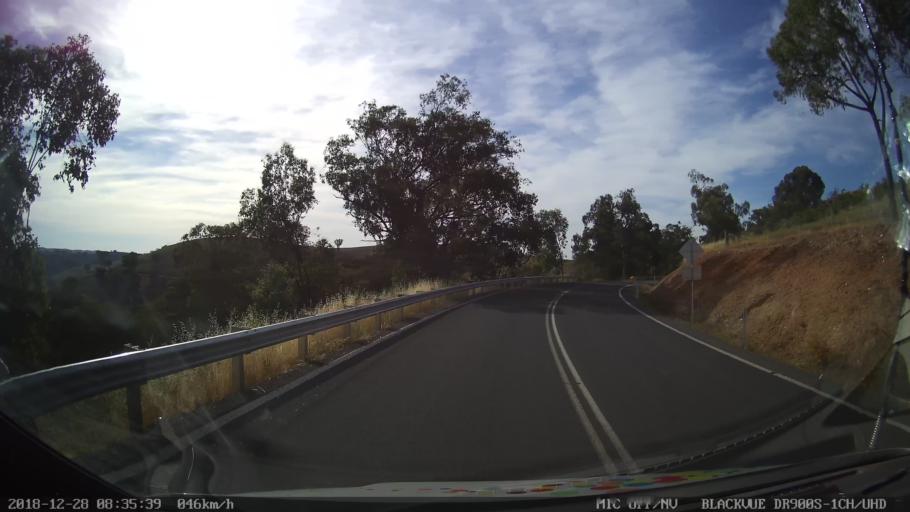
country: AU
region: New South Wales
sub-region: Blayney
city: Blayney
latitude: -33.9843
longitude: 149.3103
